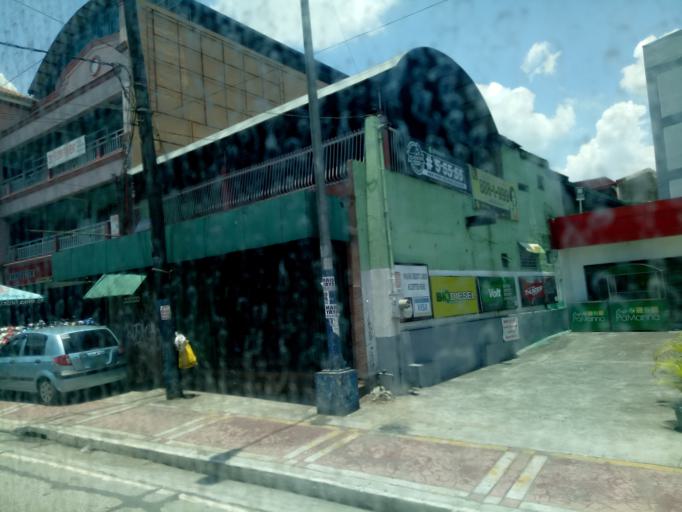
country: PH
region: Calabarzon
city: Bagong Pagasa
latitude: 14.7330
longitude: 121.0503
